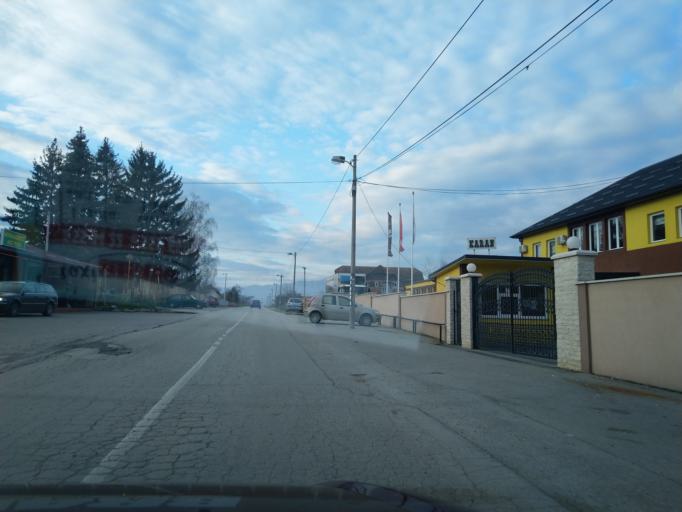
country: RS
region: Central Serbia
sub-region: Zlatiborski Okrug
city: Kosjeric
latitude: 43.9183
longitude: 19.9085
